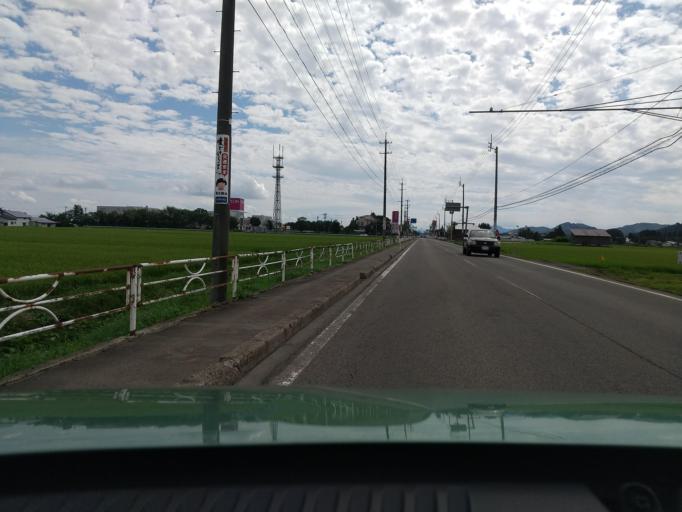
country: JP
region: Akita
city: Kakunodatemachi
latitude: 39.5550
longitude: 140.5524
